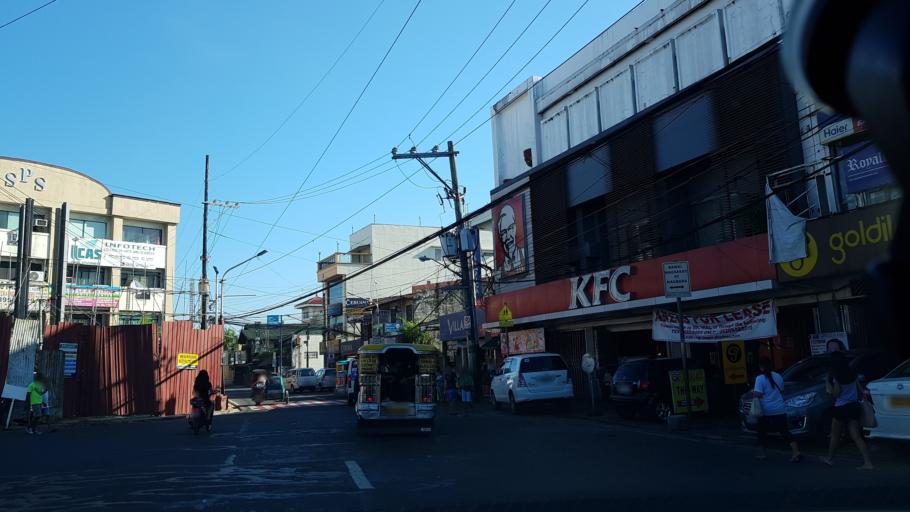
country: PH
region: Calabarzon
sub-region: Province of Rizal
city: Pateros
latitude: 14.5613
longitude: 121.0766
